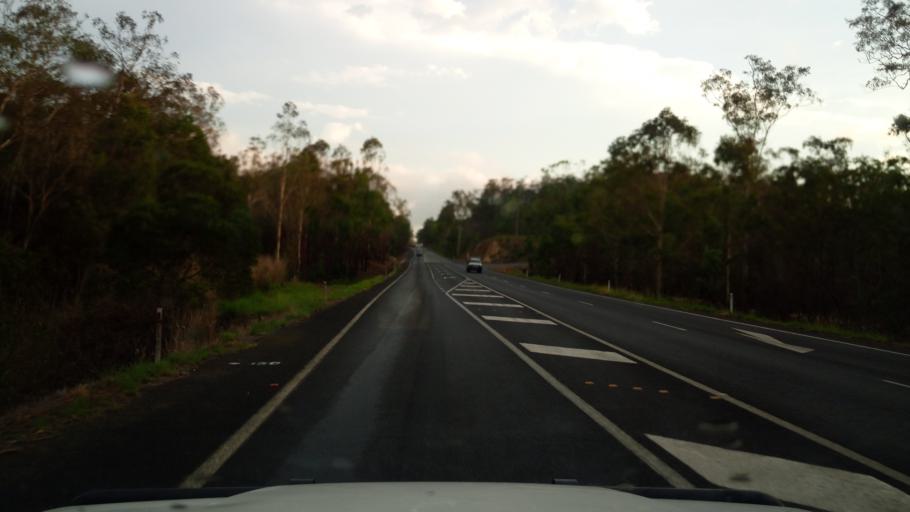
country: AU
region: Queensland
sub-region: Tablelands
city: Kuranda
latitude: -16.8535
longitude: 145.6011
